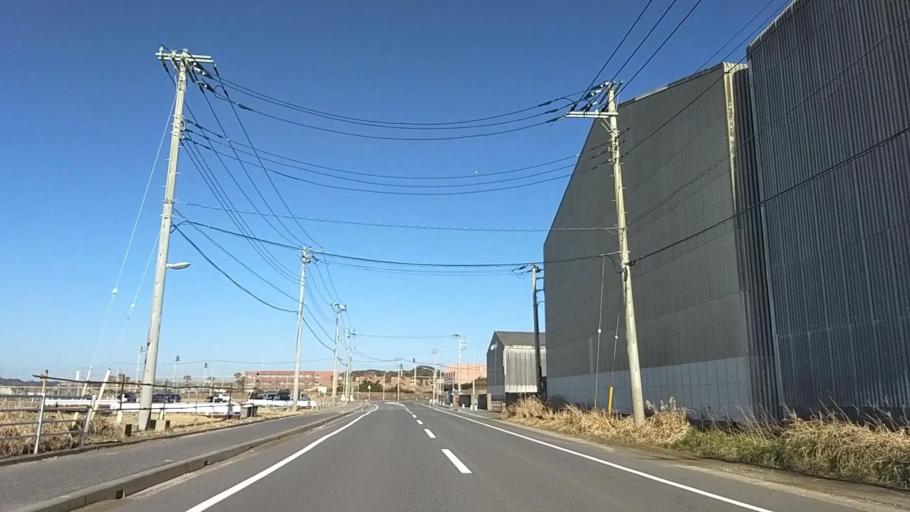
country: JP
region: Chiba
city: Hasaki
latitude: 35.7024
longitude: 140.8448
